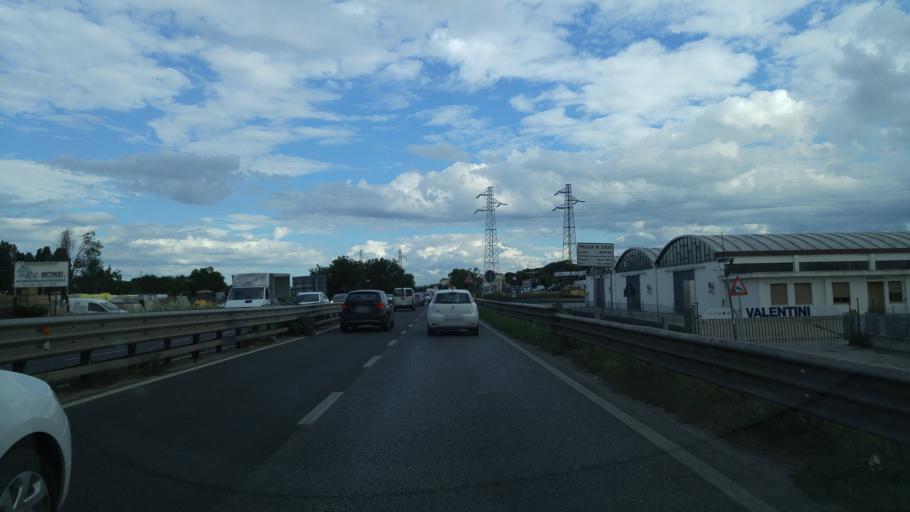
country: IT
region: Emilia-Romagna
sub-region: Provincia di Rimini
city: Rimini
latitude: 44.0517
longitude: 12.5467
